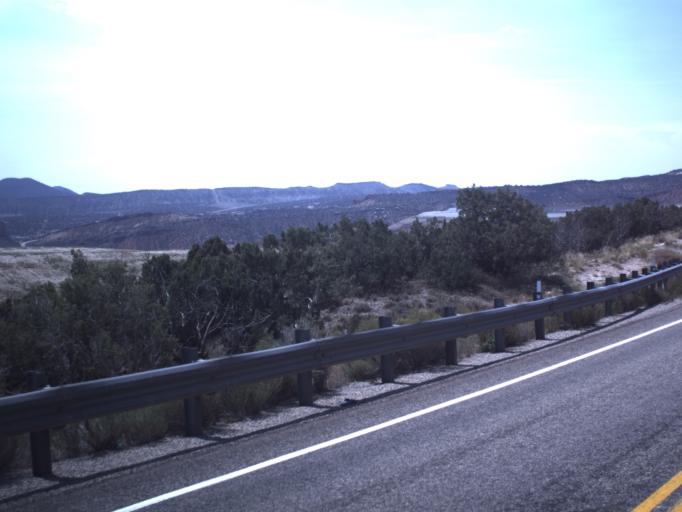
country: US
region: Utah
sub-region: Uintah County
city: Vernal
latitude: 40.6137
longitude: -109.4727
